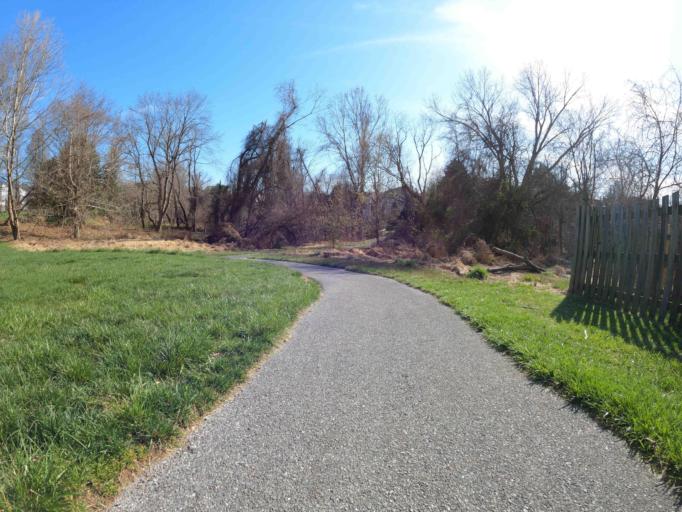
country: US
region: Maryland
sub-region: Howard County
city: Ellicott City
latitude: 39.3037
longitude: -76.8104
